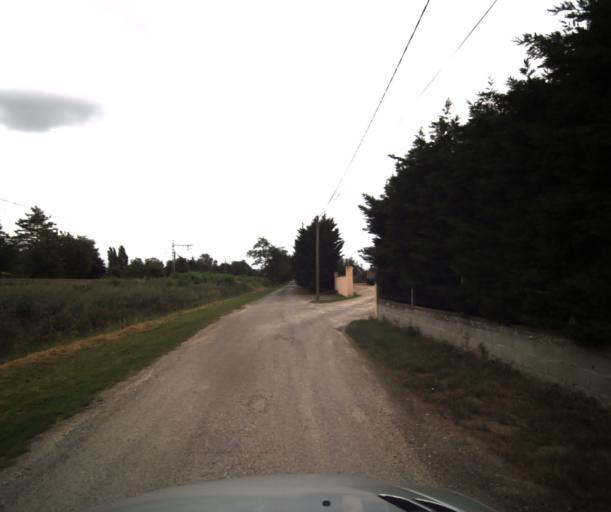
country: FR
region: Midi-Pyrenees
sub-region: Departement de la Haute-Garonne
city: Labarthe-sur-Leze
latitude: 43.4537
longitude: 1.4142
